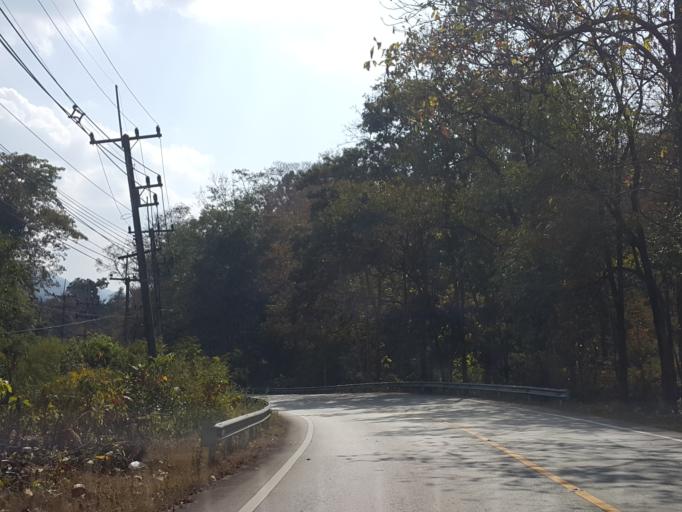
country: TH
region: Chiang Mai
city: Hot
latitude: 18.2099
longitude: 98.4472
